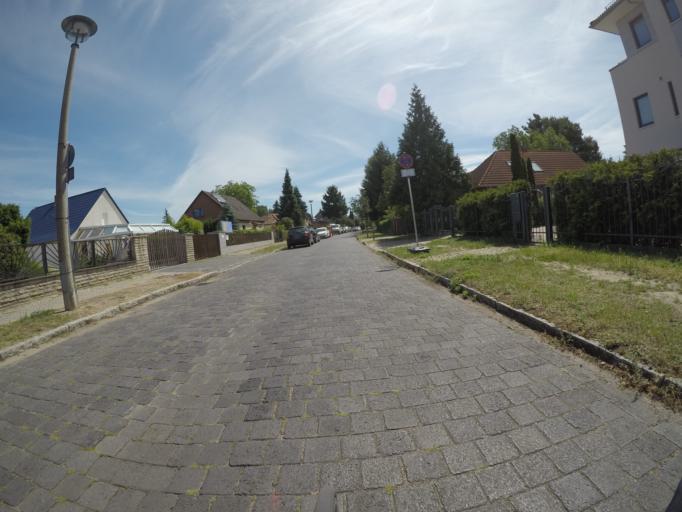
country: DE
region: Berlin
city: Kaulsdorf
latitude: 52.4971
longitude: 13.5806
